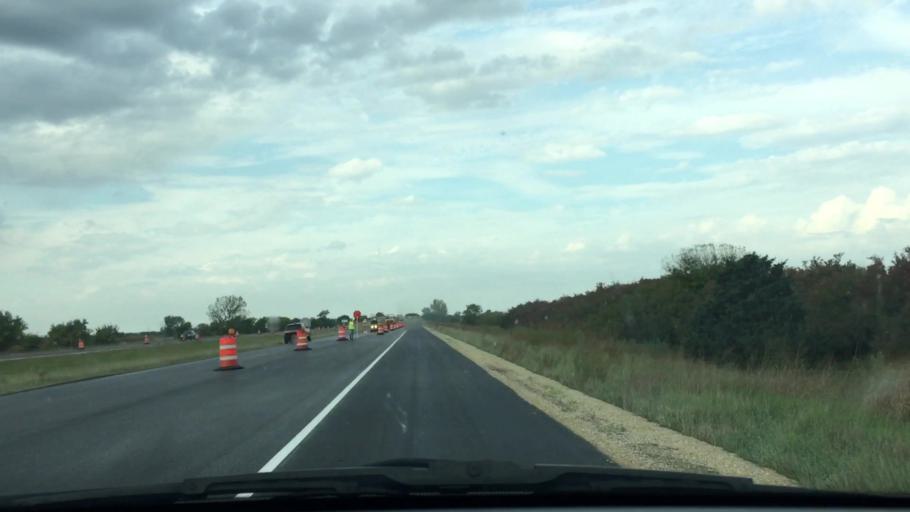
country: US
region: Illinois
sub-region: Whiteside County
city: Prophetstown
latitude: 41.7178
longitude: -89.9869
